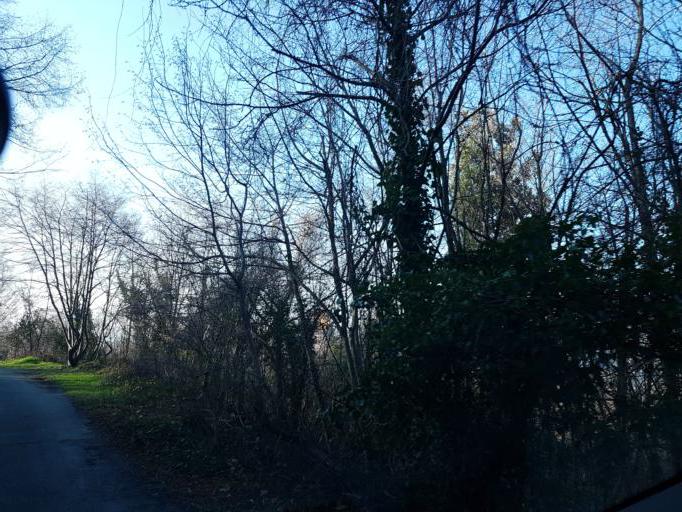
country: IT
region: Liguria
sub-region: Provincia di Genova
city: Manesseno
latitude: 44.4592
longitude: 8.9253
